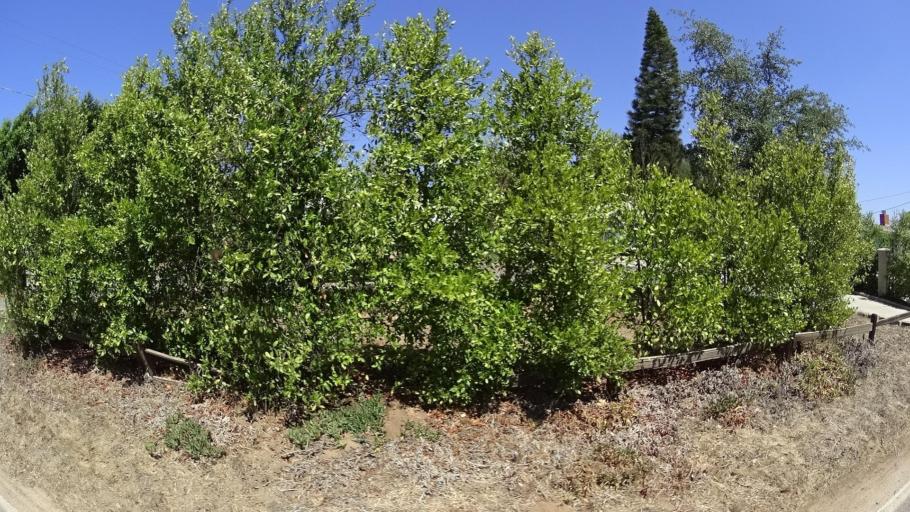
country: US
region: California
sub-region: San Diego County
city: Fallbrook
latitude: 33.3802
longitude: -117.2208
